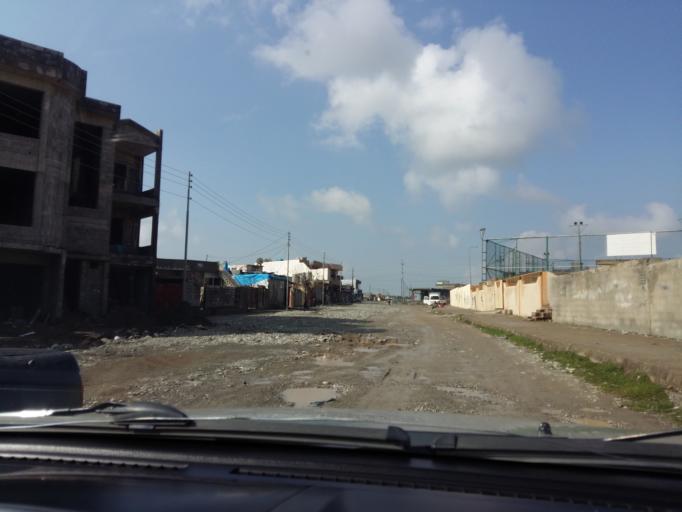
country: IQ
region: As Sulaymaniyah
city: Qeladize
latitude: 36.1931
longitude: 45.1291
